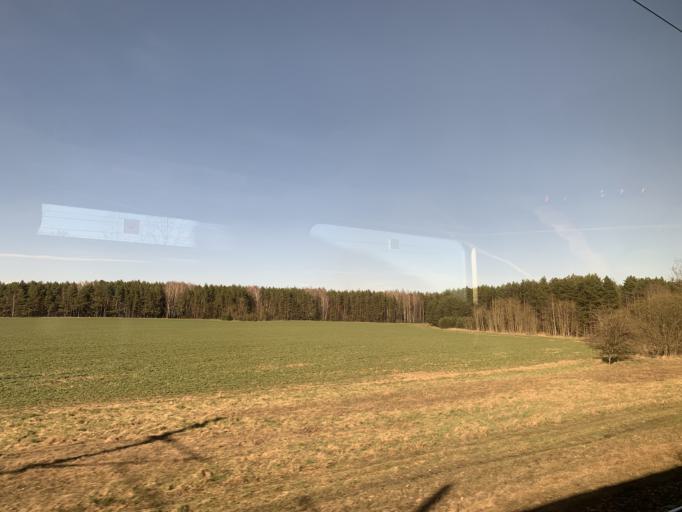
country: BY
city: Soly
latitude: 54.4937
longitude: 26.2807
